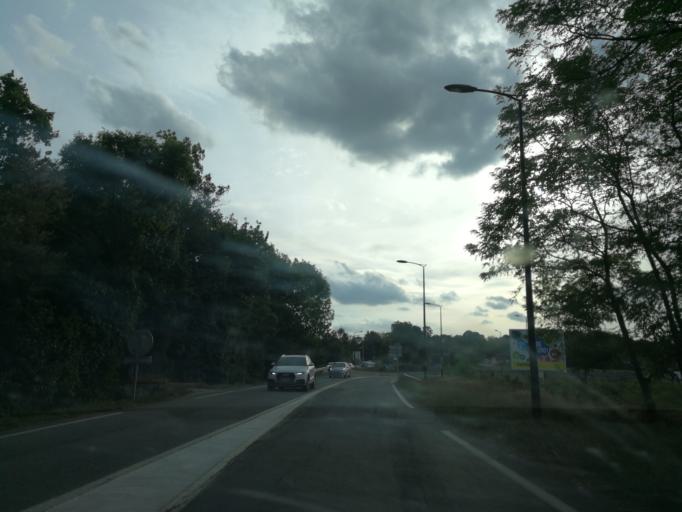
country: FR
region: Midi-Pyrenees
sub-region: Departement de la Haute-Garonne
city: Flourens
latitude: 43.5878
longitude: 1.5810
